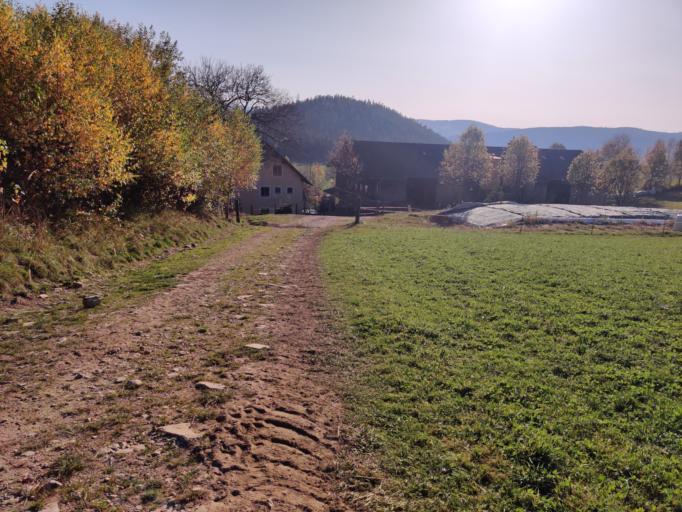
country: AT
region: Styria
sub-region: Politischer Bezirk Hartberg-Fuerstenfeld
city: Sankt Jakob im Walde
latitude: 47.4670
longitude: 15.8099
